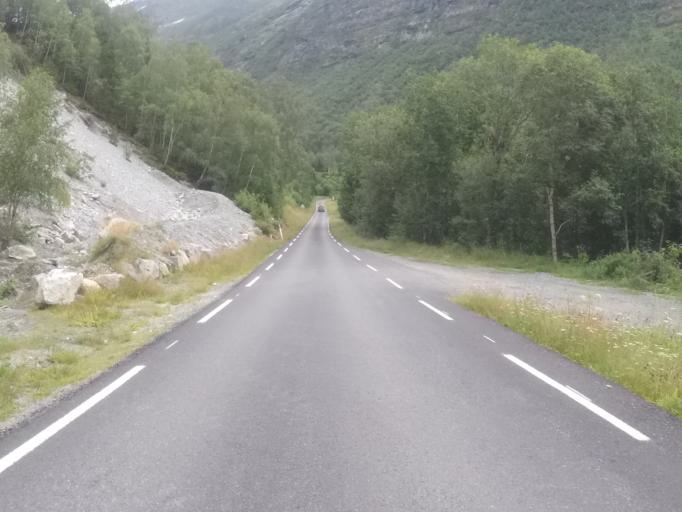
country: NO
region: Sogn og Fjordane
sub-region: Stryn
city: Stryn
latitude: 61.8035
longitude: 7.0071
